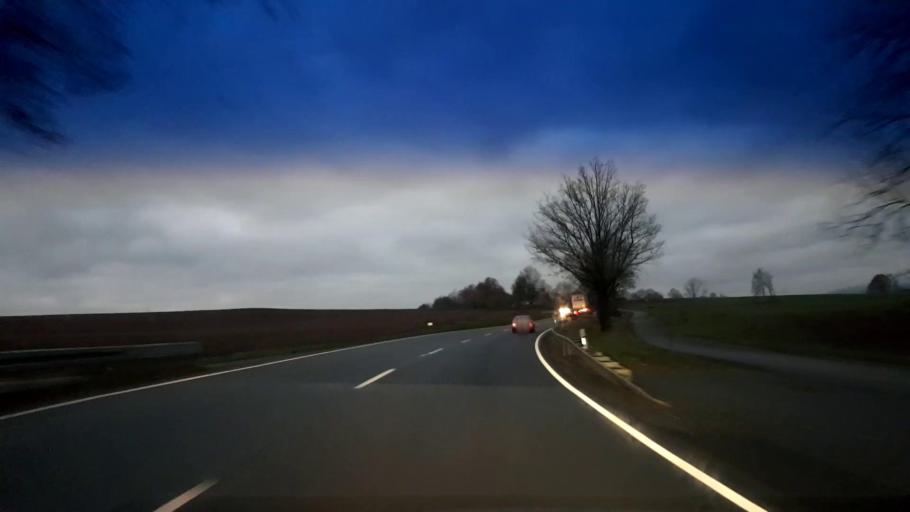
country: DE
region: Bavaria
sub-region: Upper Palatinate
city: Kemnath
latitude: 49.8654
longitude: 11.9109
